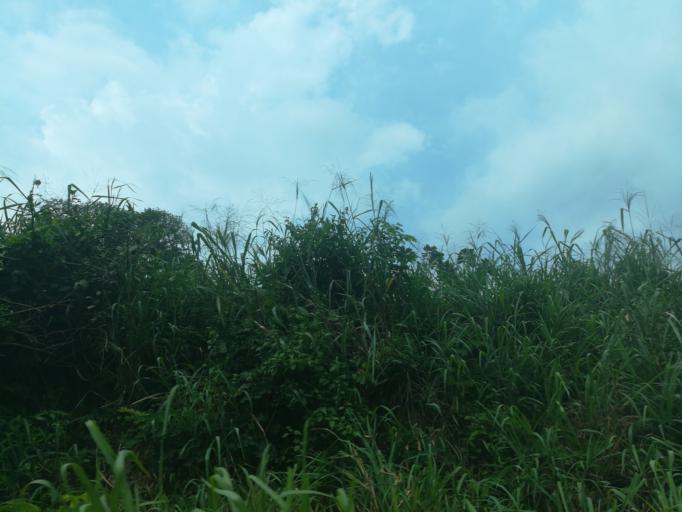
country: NG
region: Lagos
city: Ikorodu
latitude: 6.6720
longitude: 3.6617
